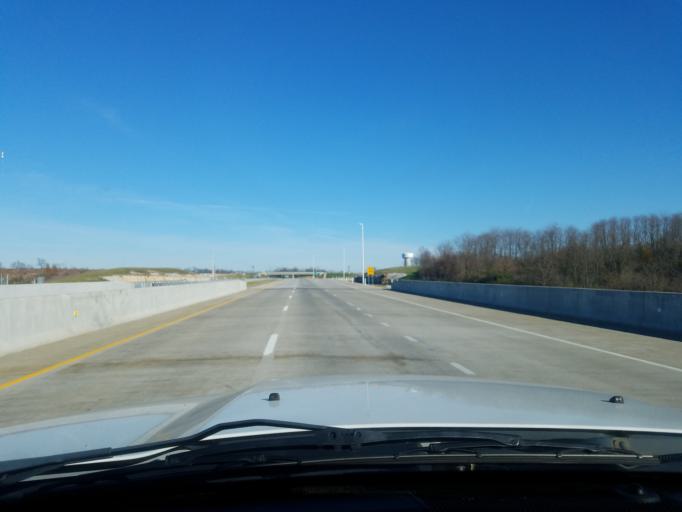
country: US
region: Indiana
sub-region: Clark County
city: Oak Park
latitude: 38.3472
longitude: -85.6737
